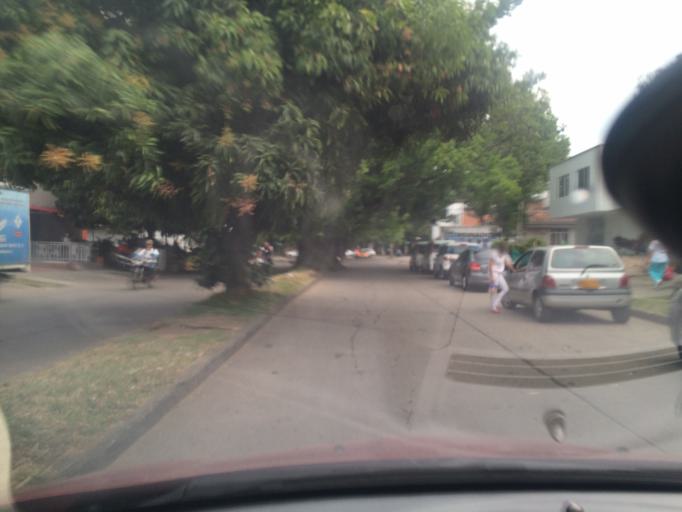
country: CO
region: Valle del Cauca
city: Cali
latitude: 3.4198
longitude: -76.5451
